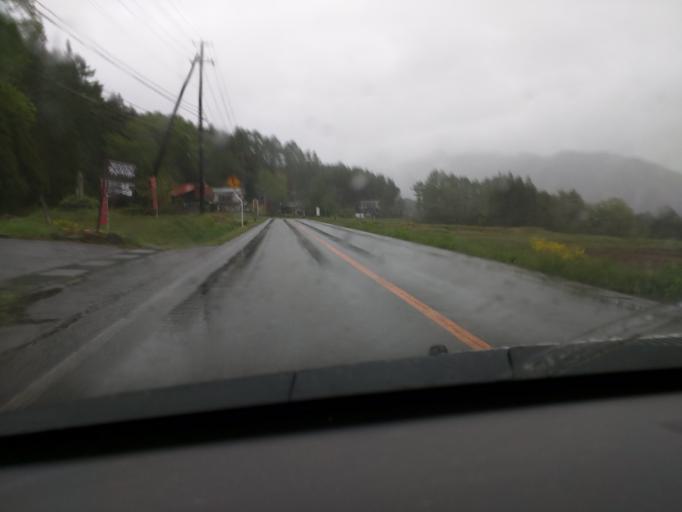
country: JP
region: Fukushima
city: Inawashiro
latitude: 37.5900
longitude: 140.1253
